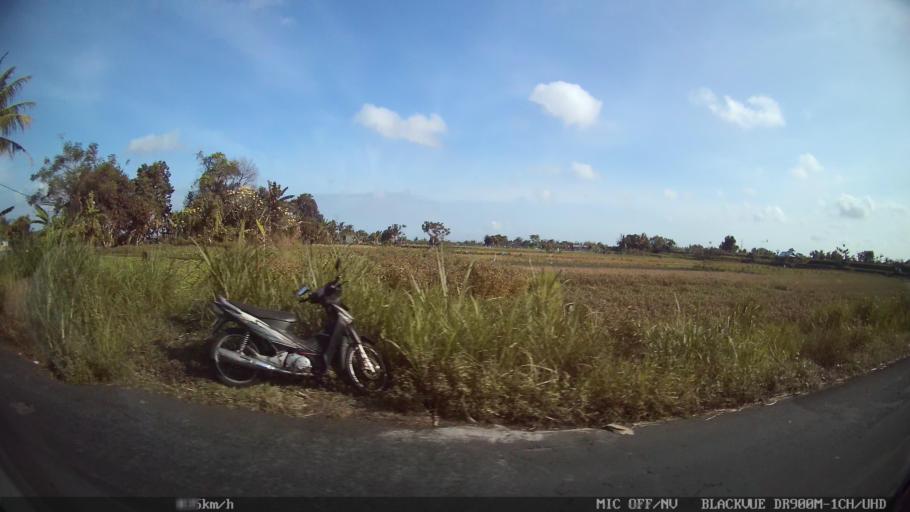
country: ID
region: Bali
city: Banjar Parekan
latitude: -8.5796
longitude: 115.2249
